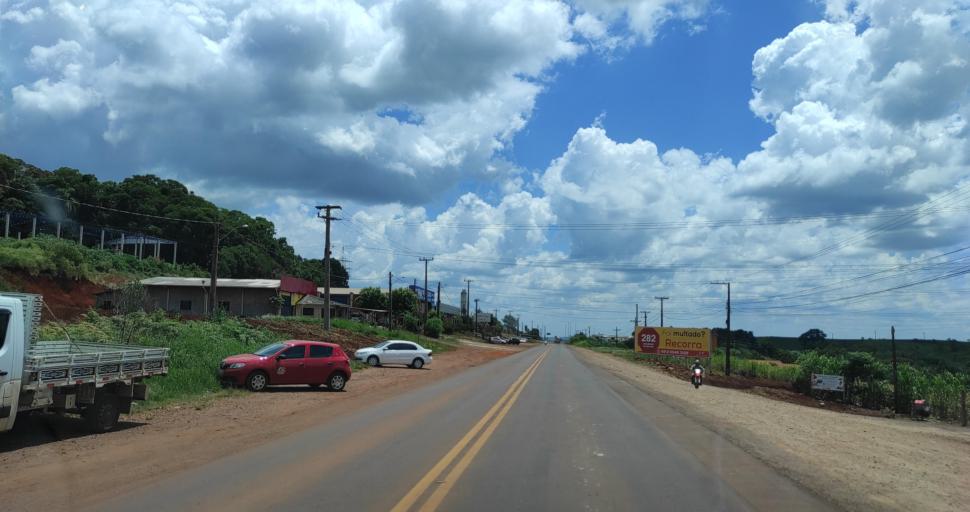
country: BR
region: Santa Catarina
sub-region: Xanxere
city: Xanxere
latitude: -26.8554
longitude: -52.4045
